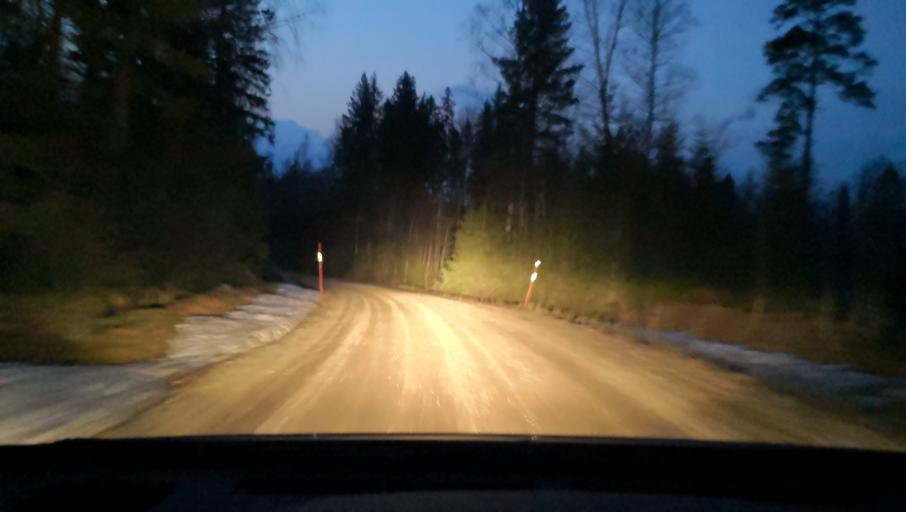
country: SE
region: OErebro
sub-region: Lindesbergs Kommun
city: Frovi
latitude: 59.6234
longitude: 15.4802
